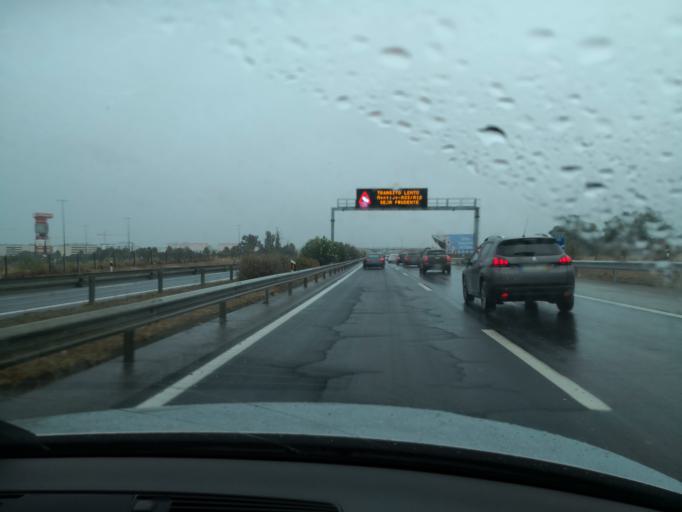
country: PT
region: Setubal
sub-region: Montijo
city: Montijo
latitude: 38.6944
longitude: -8.9391
